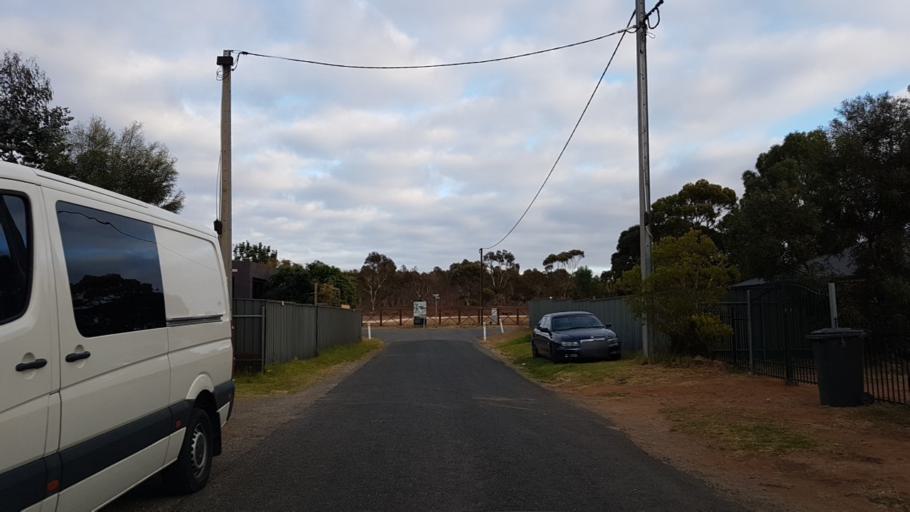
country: AU
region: South Australia
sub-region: Mount Barker
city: Callington
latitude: -35.1161
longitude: 139.0355
